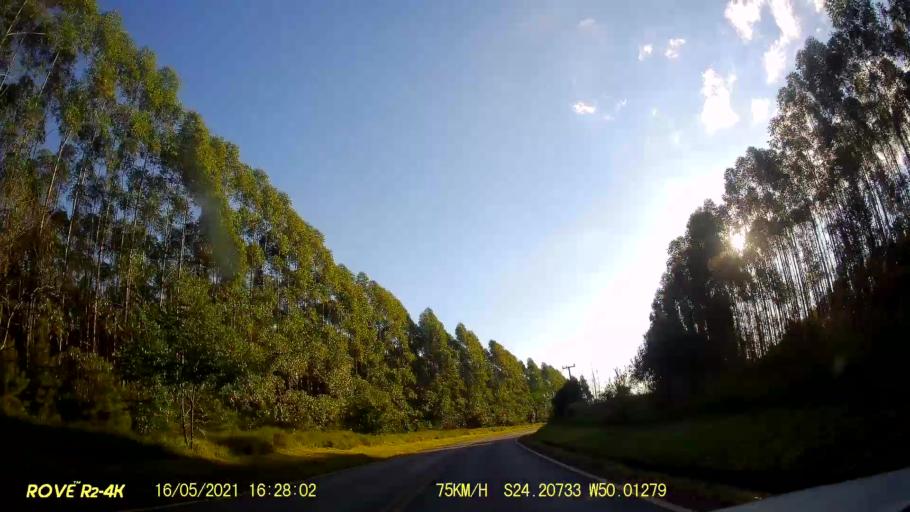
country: BR
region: Parana
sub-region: Jaguariaiva
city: Jaguariaiva
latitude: -24.2073
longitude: -50.0129
